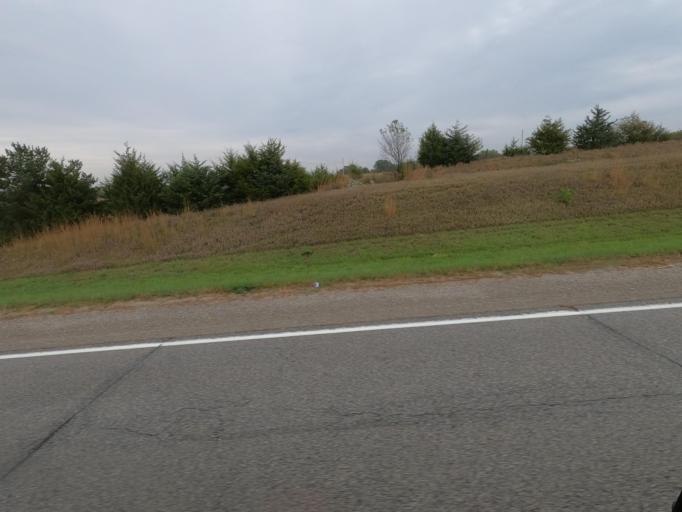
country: US
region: Iowa
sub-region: Van Buren County
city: Keosauqua
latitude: 40.8468
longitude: -92.0312
